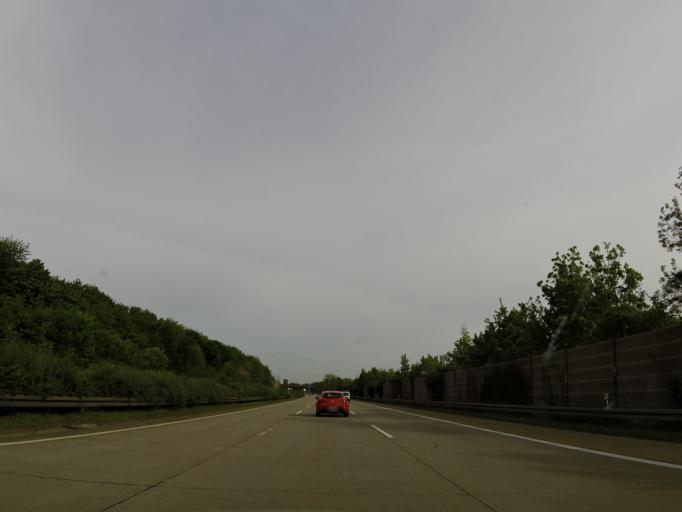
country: DE
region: Lower Saxony
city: Hildesheim
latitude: 52.1703
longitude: 9.9831
